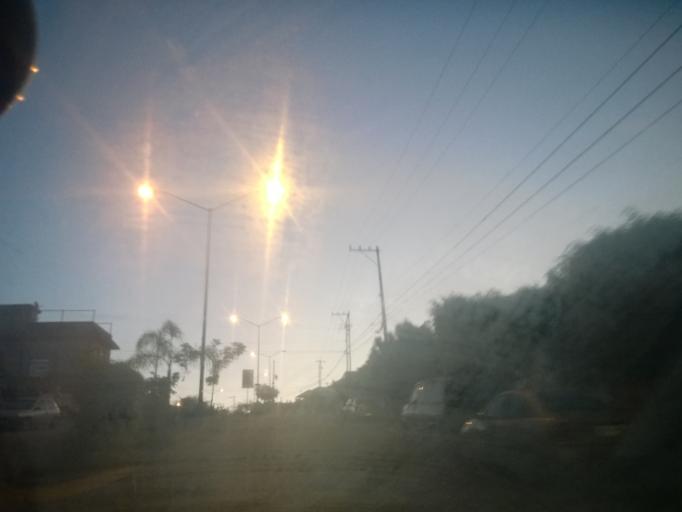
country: MX
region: Guanajuato
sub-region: Leon
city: La Ermita
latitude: 21.1586
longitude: -101.7351
